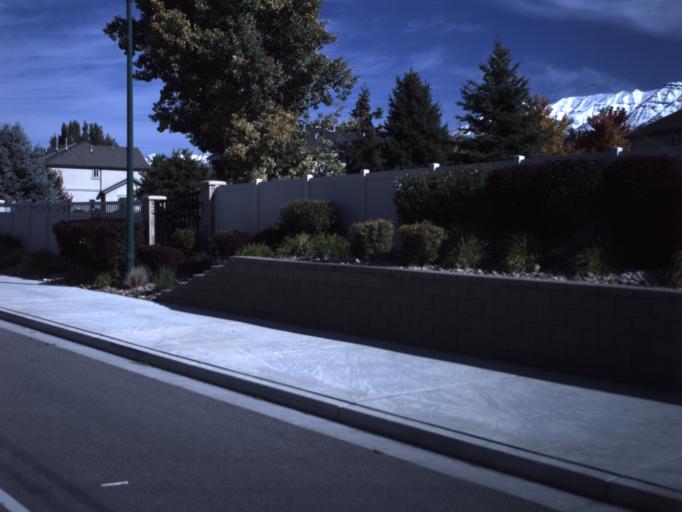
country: US
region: Utah
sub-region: Utah County
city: Orem
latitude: 40.2833
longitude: -111.7327
